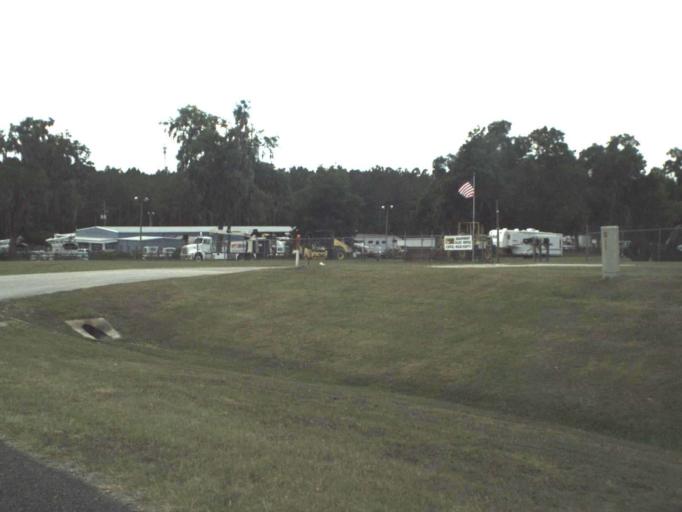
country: US
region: Florida
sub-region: Marion County
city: Ocala
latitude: 29.2452
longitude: -82.1523
